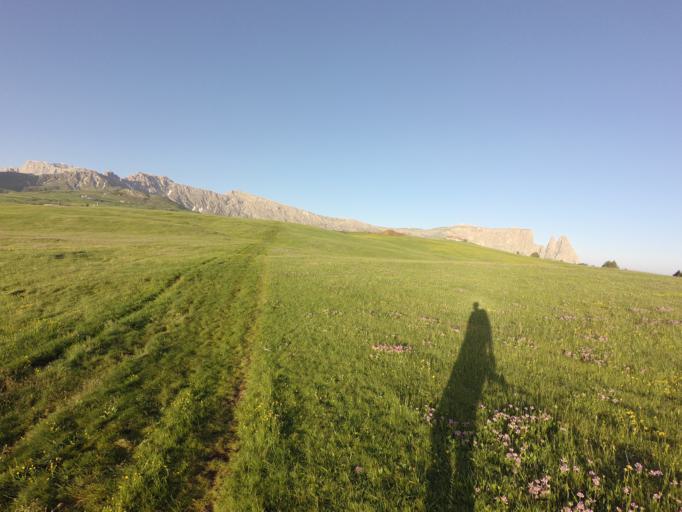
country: IT
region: Trentino-Alto Adige
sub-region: Bolzano
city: Ortisei
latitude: 46.5359
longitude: 11.6372
